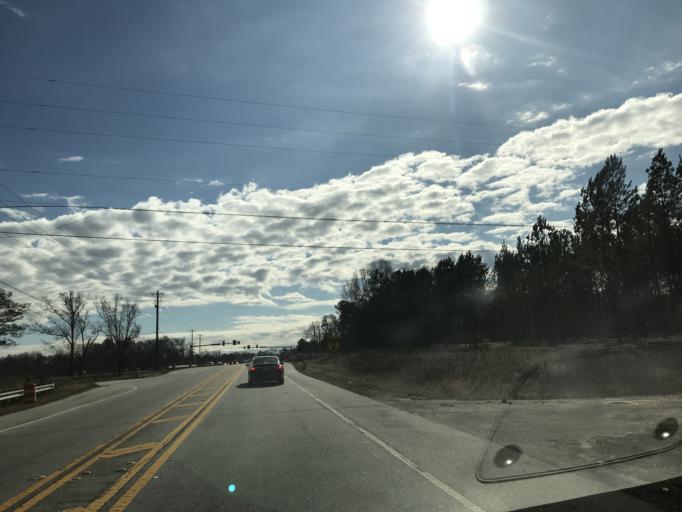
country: US
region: Georgia
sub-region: Paulding County
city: Hiram
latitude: 33.8583
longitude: -84.7593
